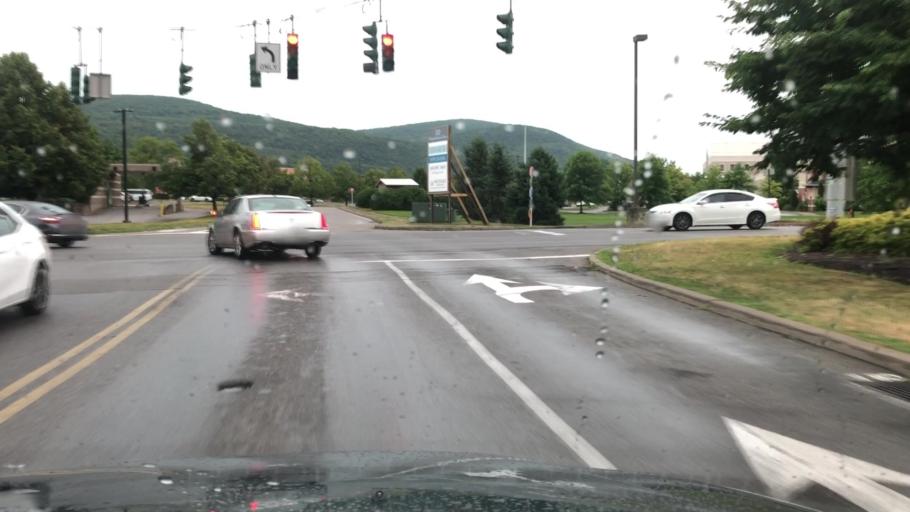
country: US
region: New York
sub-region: Dutchess County
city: Fishkill
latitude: 41.5295
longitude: -73.8961
